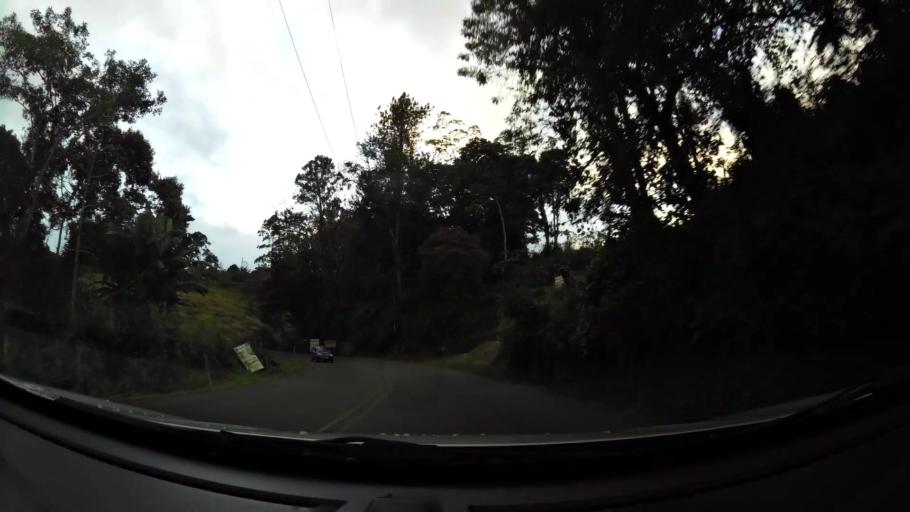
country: CR
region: Cartago
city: Turrialba
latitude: 9.9003
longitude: -83.6890
